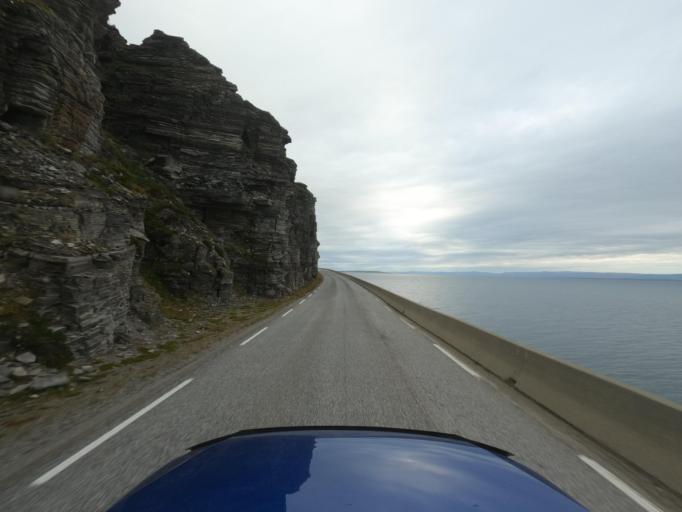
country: NO
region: Finnmark Fylke
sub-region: Nordkapp
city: Honningsvag
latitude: 70.6807
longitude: 25.4836
